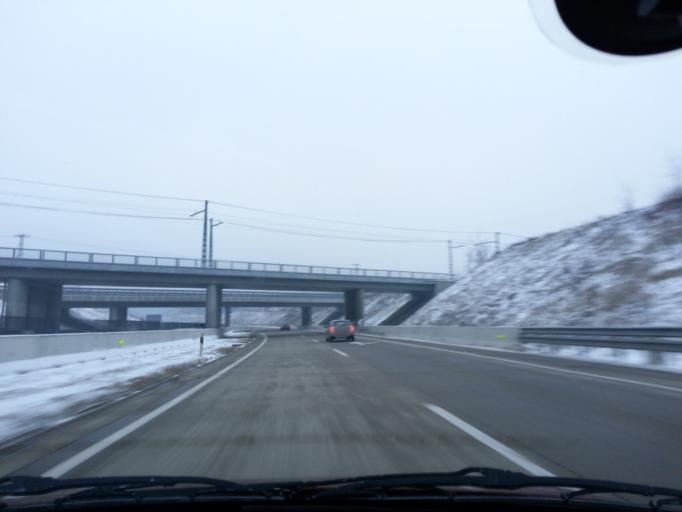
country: HU
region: Pest
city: Godollo
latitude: 47.5908
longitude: 19.3135
